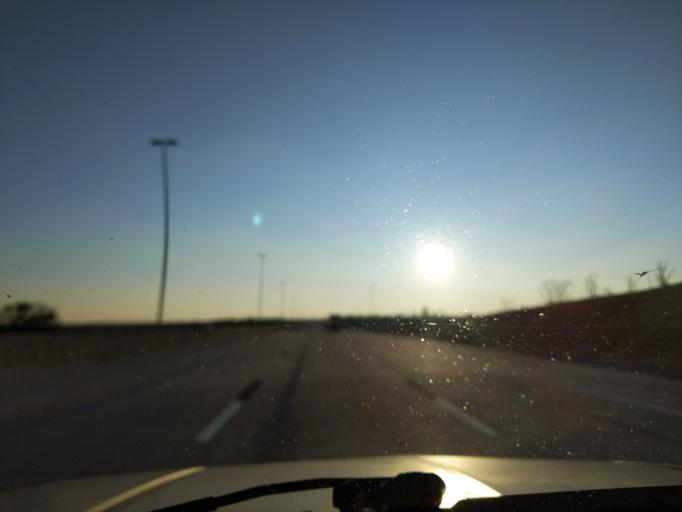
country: US
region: Oklahoma
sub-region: Creek County
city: Kellyville
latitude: 35.9500
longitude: -96.2458
